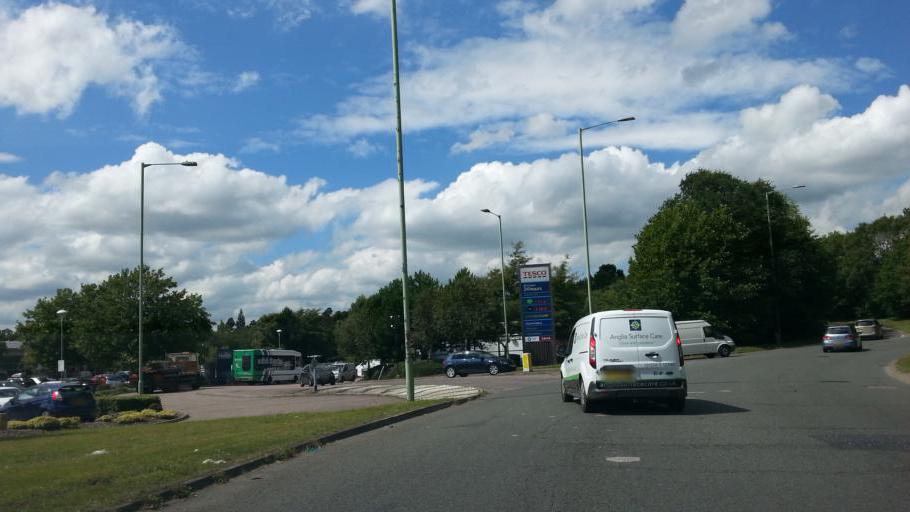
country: GB
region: England
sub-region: Suffolk
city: Bury St Edmunds
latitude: 52.2545
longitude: 0.7176
